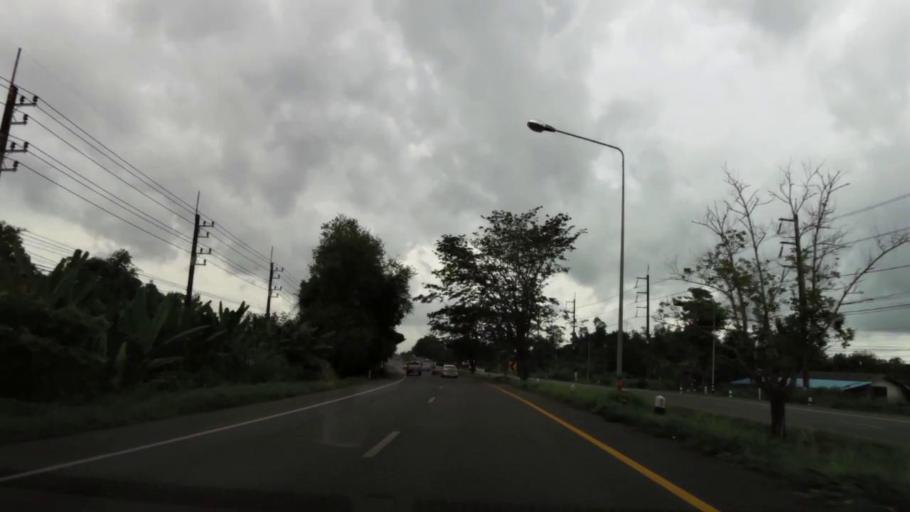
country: TH
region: Chanthaburi
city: Tha Mai
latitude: 12.6831
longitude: 102.0044
